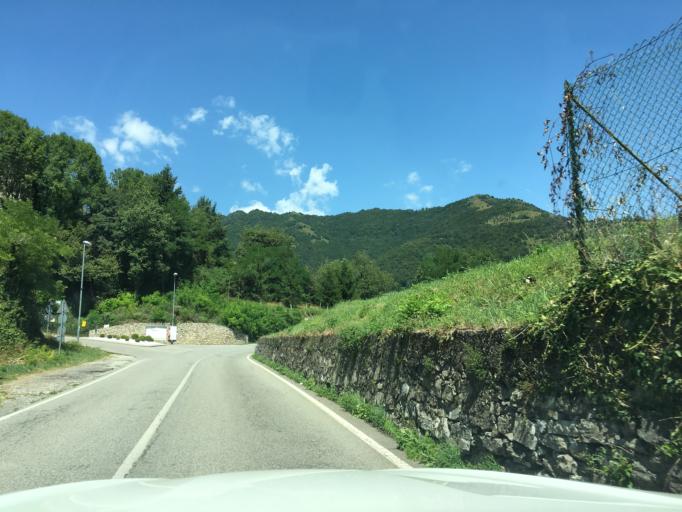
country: IT
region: Lombardy
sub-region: Provincia di Bergamo
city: Nembro
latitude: 45.7487
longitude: 9.7590
